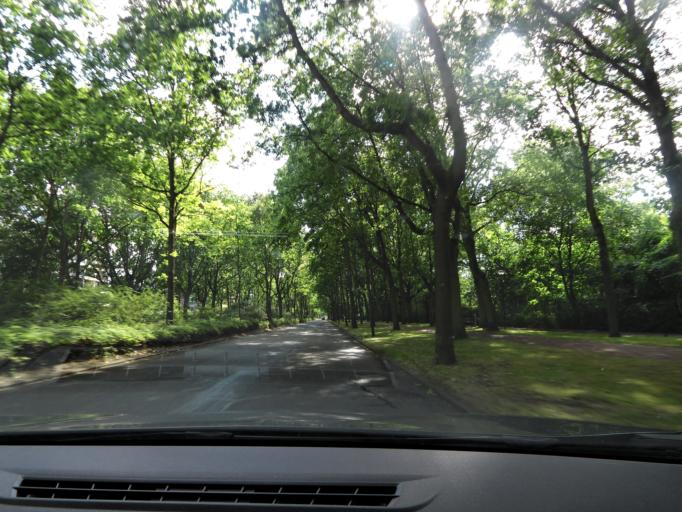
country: NL
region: South Holland
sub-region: Gemeente Rijswijk
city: Rijswijk
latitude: 52.0451
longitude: 4.3258
